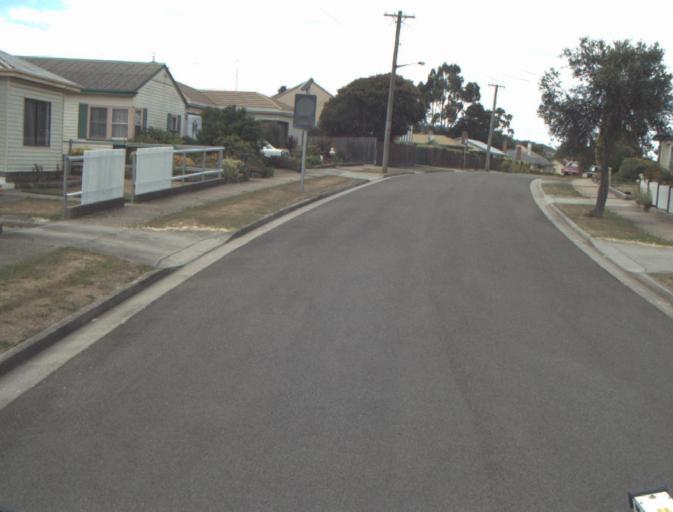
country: AU
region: Tasmania
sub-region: Launceston
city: Newstead
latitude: -41.4381
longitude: 147.1638
